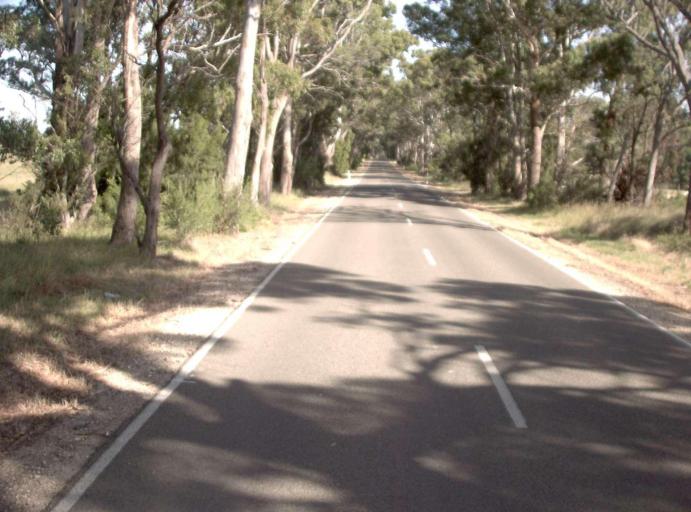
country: AU
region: Victoria
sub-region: East Gippsland
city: Lakes Entrance
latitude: -37.8094
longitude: 147.8439
